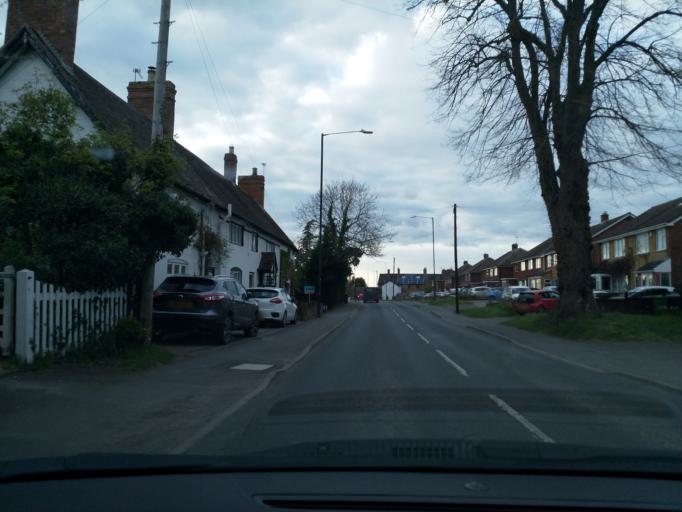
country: GB
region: England
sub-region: Warwickshire
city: Royal Leamington Spa
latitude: 52.2709
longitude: -1.5218
